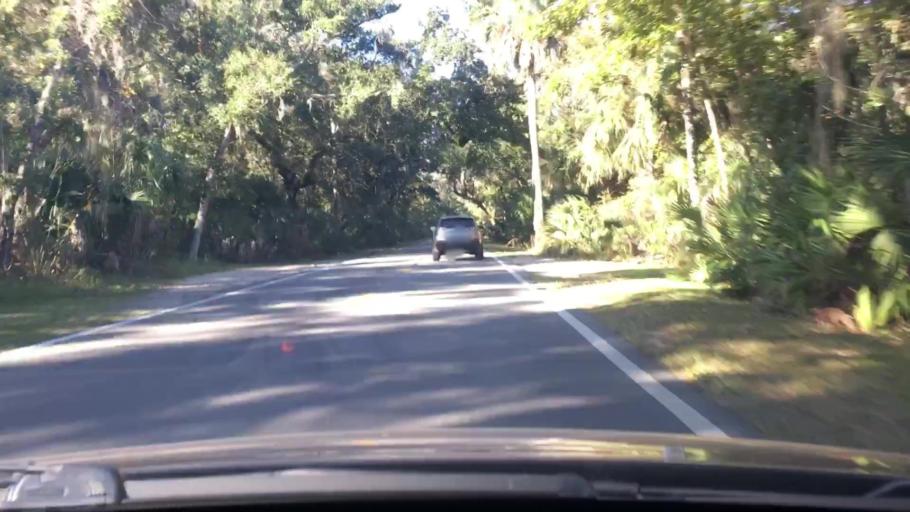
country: US
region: Florida
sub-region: Volusia County
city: Ormond-by-the-Sea
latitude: 29.3780
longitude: -81.1290
